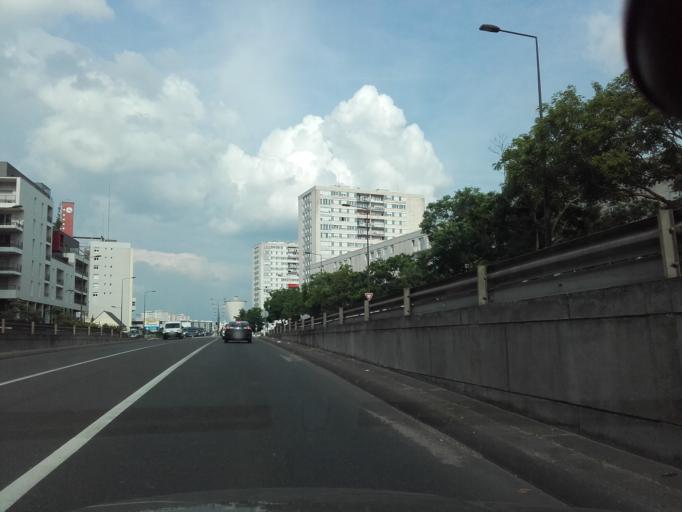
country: FR
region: Centre
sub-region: Departement d'Indre-et-Loire
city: Tours
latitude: 47.3740
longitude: 0.6968
